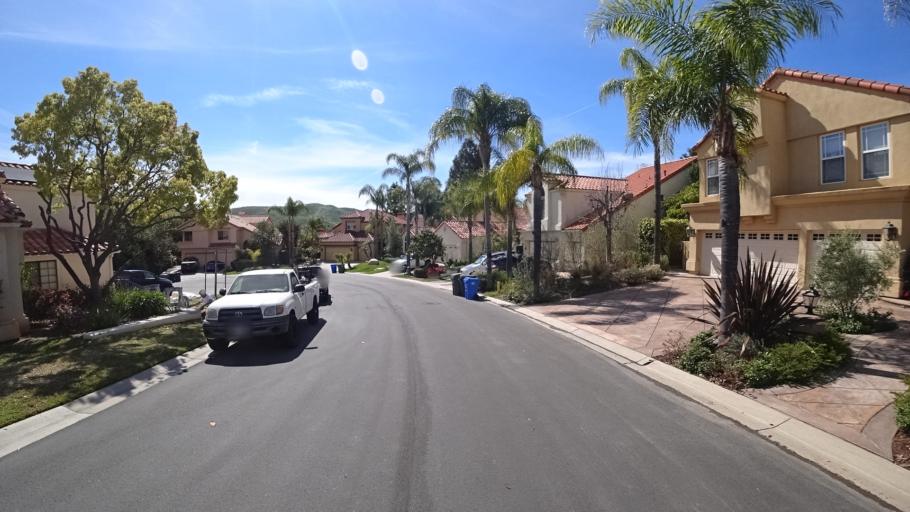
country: US
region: California
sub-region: Ventura County
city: Oak Park
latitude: 34.1766
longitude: -118.7912
